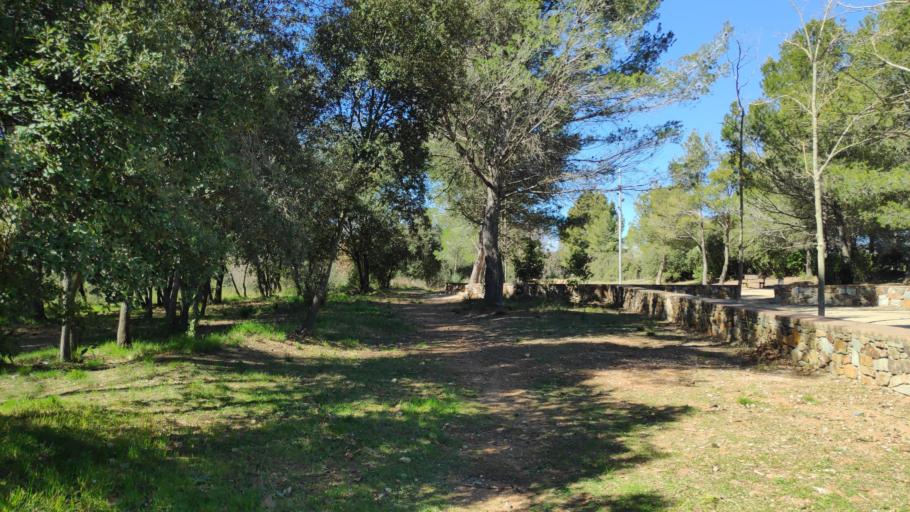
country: ES
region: Catalonia
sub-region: Provincia de Barcelona
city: Sant Quirze del Valles
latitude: 41.5638
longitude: 2.0733
